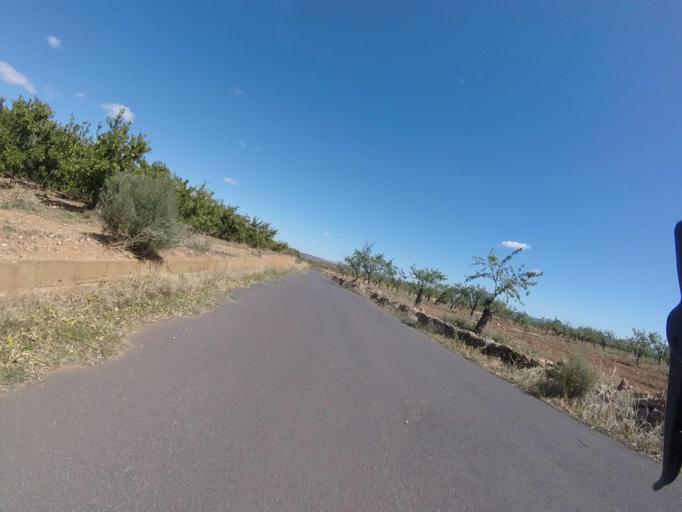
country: ES
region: Valencia
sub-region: Provincia de Castello
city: Orpesa/Oropesa del Mar
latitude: 40.1661
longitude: 0.1535
